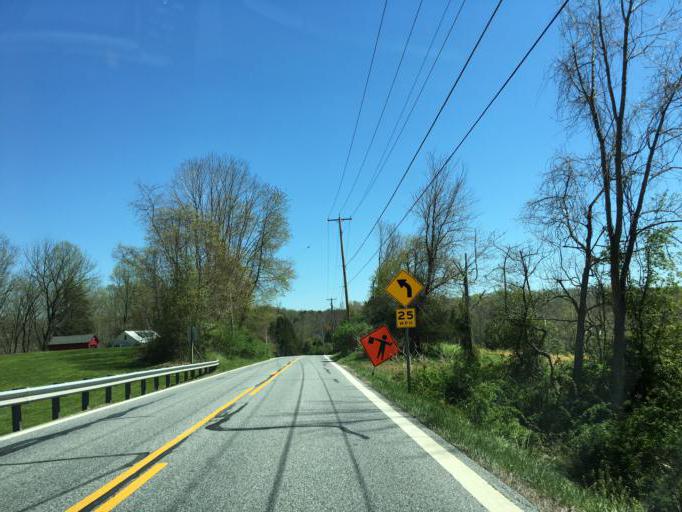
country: US
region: Maryland
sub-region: Baltimore County
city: Hunt Valley
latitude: 39.5799
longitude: -76.6215
